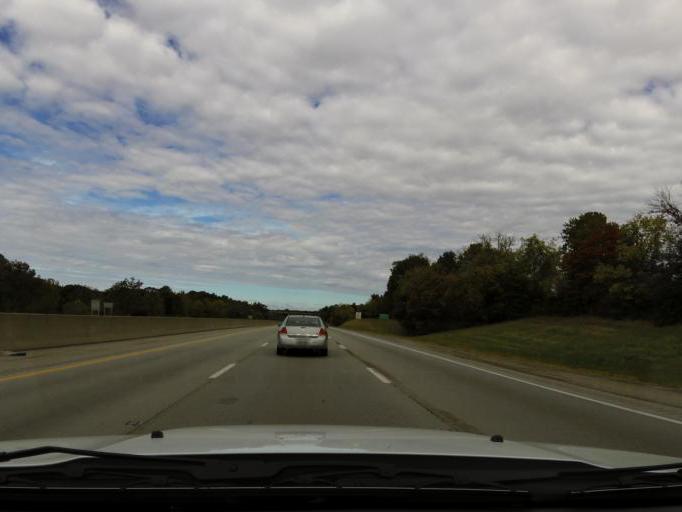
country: US
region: Kentucky
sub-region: Boone County
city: Walton
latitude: 38.8350
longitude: -84.6082
